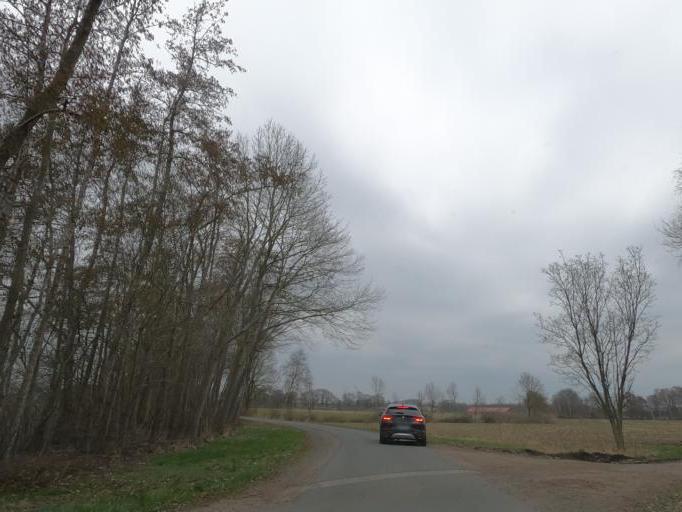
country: DE
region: Lower Saxony
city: Molbergen
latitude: 52.8680
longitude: 7.9116
